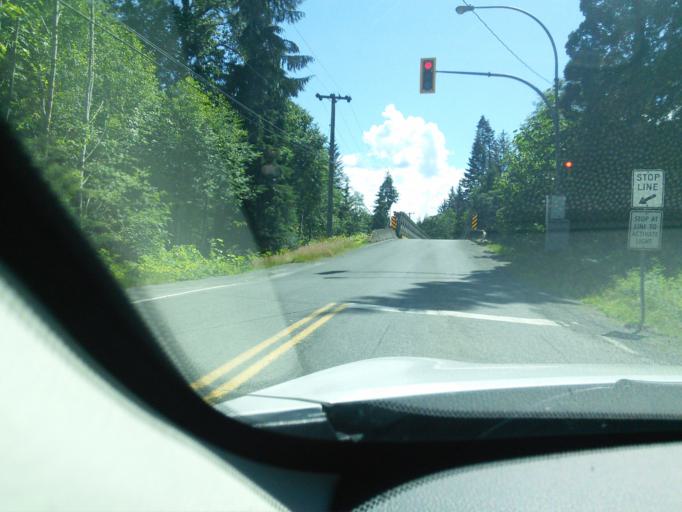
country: CA
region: British Columbia
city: Campbell River
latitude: 50.3215
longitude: -125.9221
